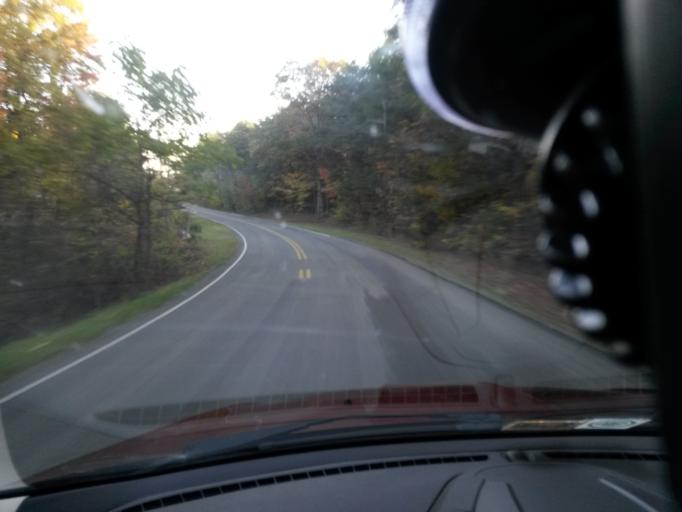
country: US
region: Virginia
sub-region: Roanoke County
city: Vinton
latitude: 37.1564
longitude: -79.8140
